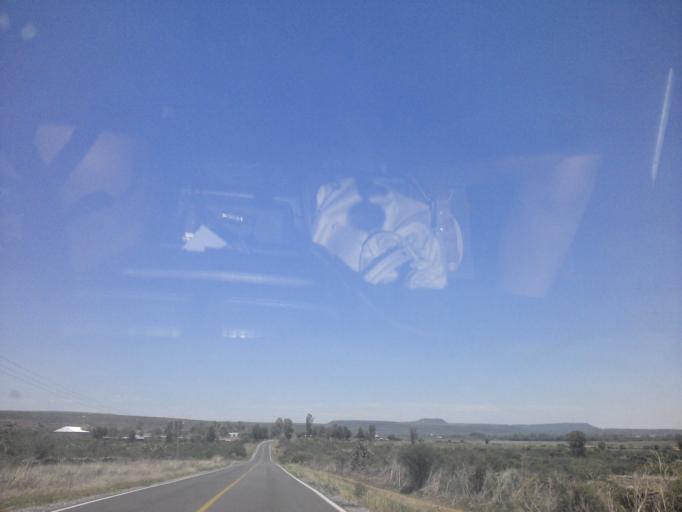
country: MX
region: Guanajuato
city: Ciudad Manuel Doblado
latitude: 20.8467
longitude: -102.0011
